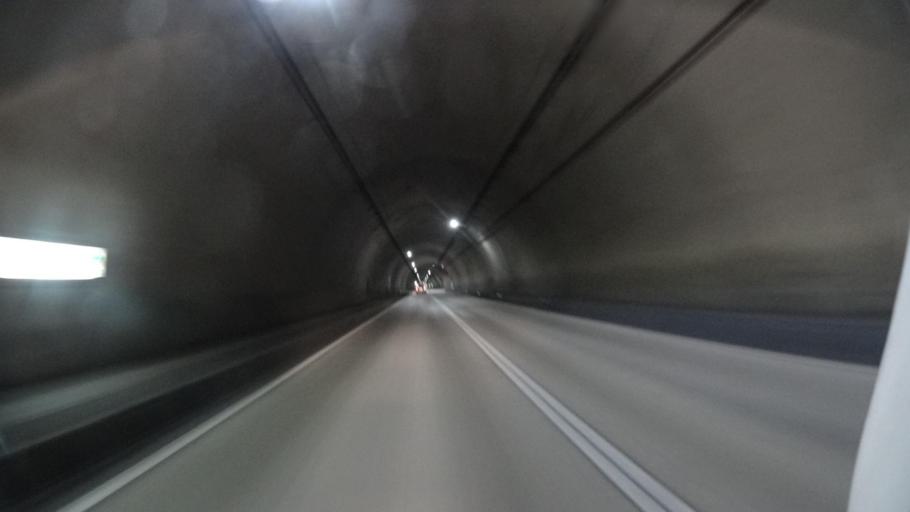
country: JP
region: Kyoto
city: Kameoka
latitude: 35.2280
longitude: 135.5737
